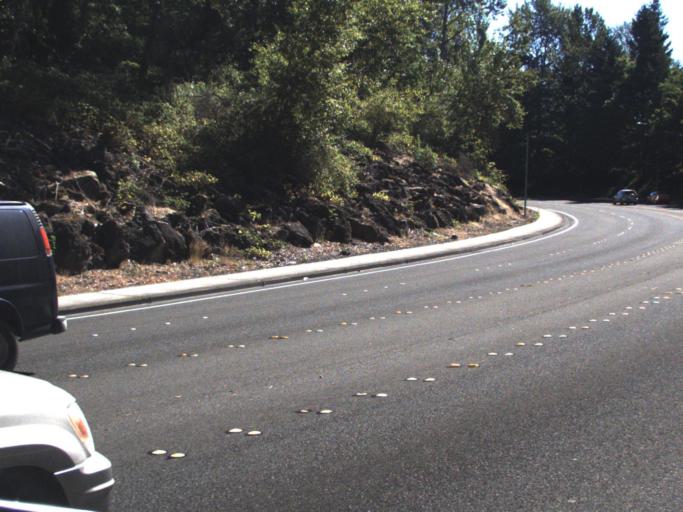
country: US
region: Washington
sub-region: King County
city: Renton
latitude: 47.5013
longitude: -122.1936
